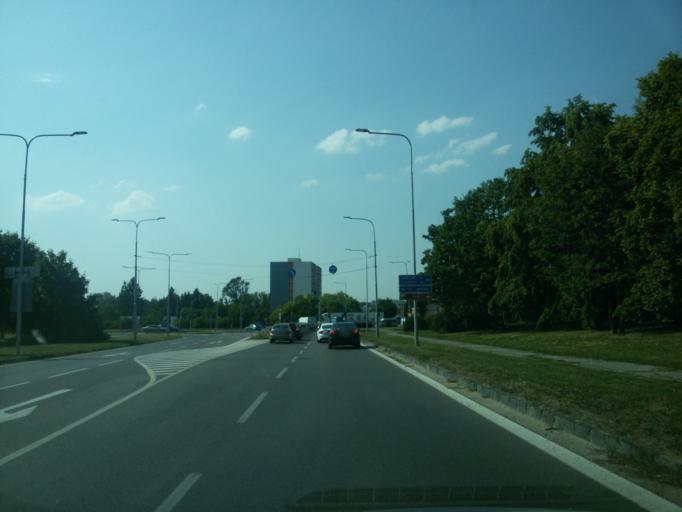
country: SK
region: Nitriansky
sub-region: Okres Nitra
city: Nitra
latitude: 48.3138
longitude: 18.1074
